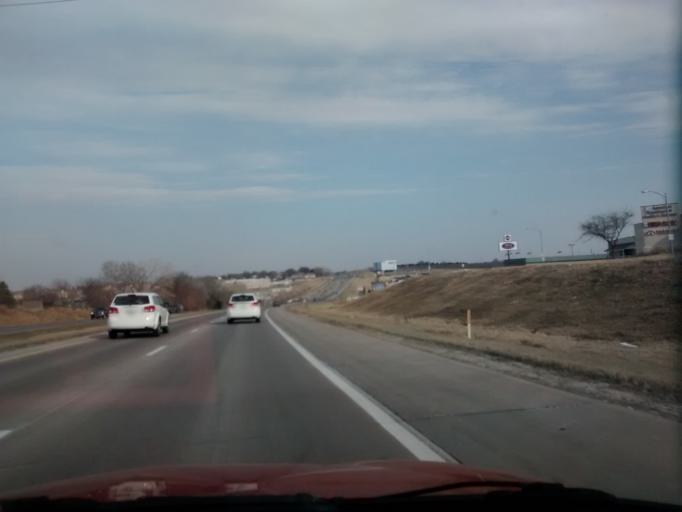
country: US
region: Nebraska
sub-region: Sarpy County
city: Papillion
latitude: 41.1398
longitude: -96.0348
